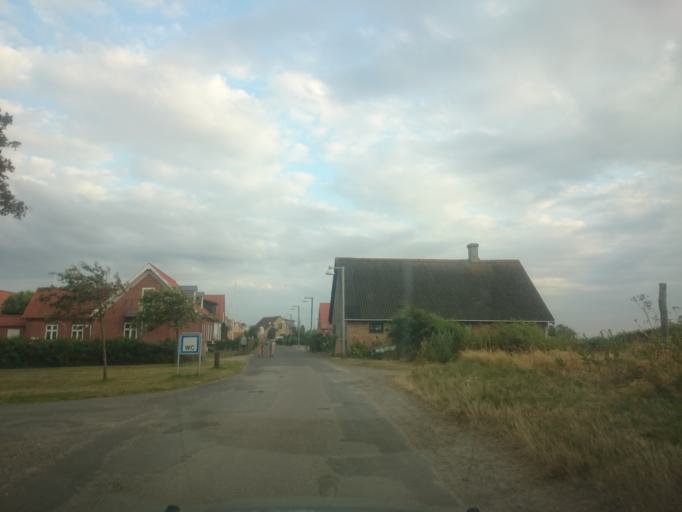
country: DK
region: South Denmark
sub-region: Nyborg Kommune
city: Nyborg
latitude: 55.1378
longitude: 10.9022
